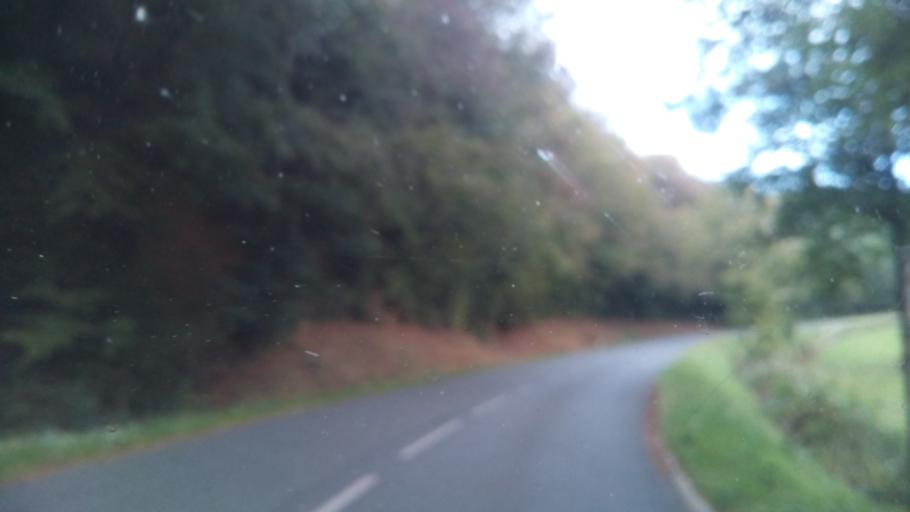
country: FR
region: Bourgogne
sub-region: Departement de Saone-et-Loire
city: Matour
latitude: 46.2256
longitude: 4.4972
